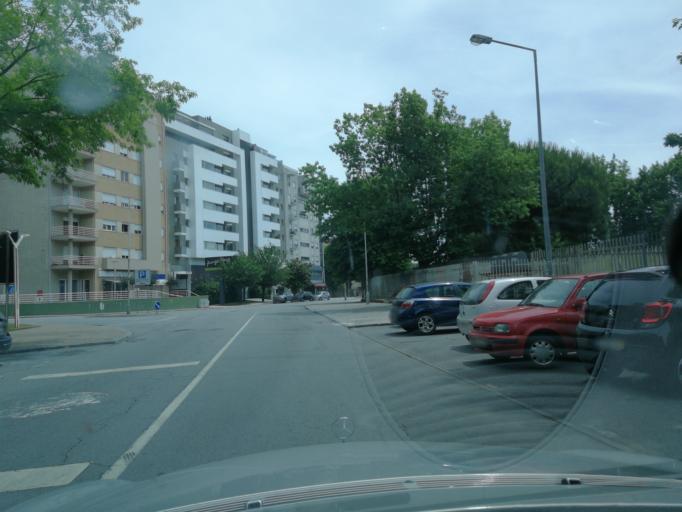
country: PT
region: Braga
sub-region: Vila Nova de Famalicao
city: Vila Nova de Famalicao
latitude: 41.4042
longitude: -8.5216
